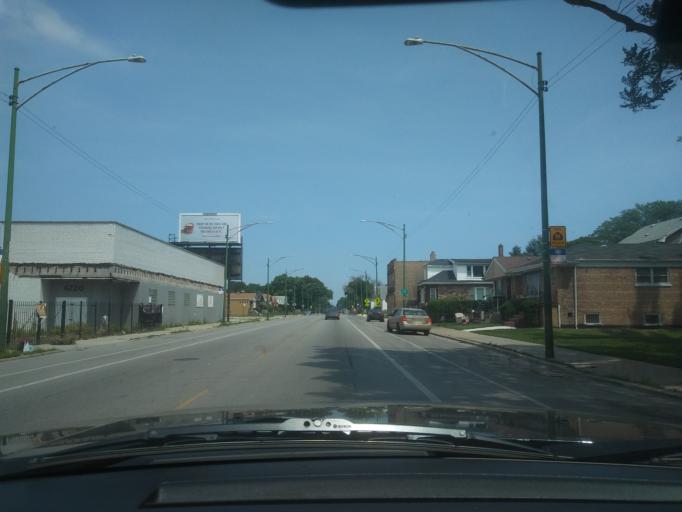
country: US
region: Illinois
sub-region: Cook County
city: Evergreen Park
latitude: 41.7801
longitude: -87.6739
